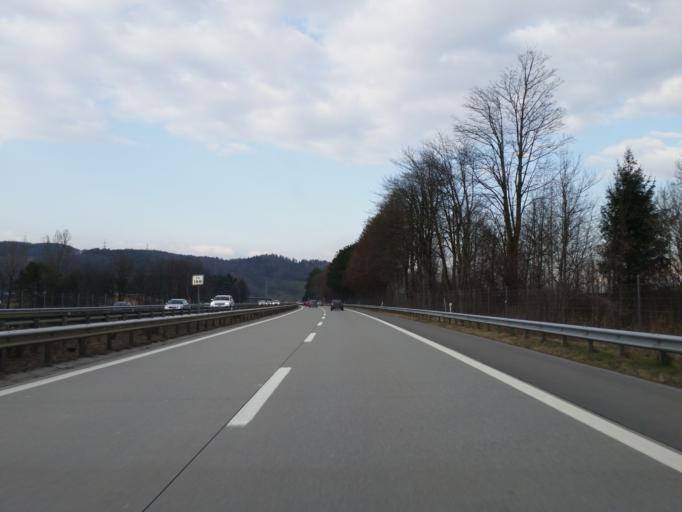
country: CH
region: Saint Gallen
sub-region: Wahlkreis Rheintal
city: Ruthi
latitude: 47.2891
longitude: 9.5507
